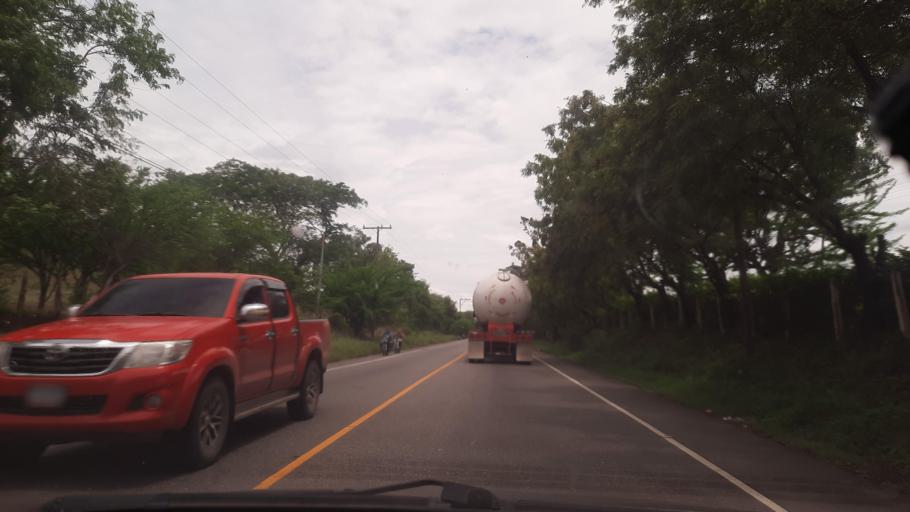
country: GT
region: Zacapa
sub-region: Municipio de Zacapa
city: Gualan
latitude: 15.0867
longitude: -89.4555
